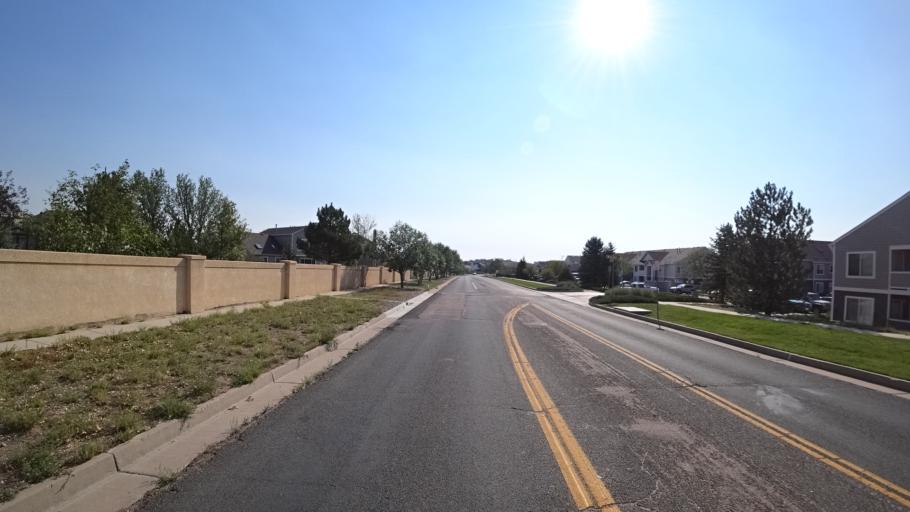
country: US
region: Colorado
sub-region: El Paso County
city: Stratmoor
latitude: 38.7680
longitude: -104.8074
